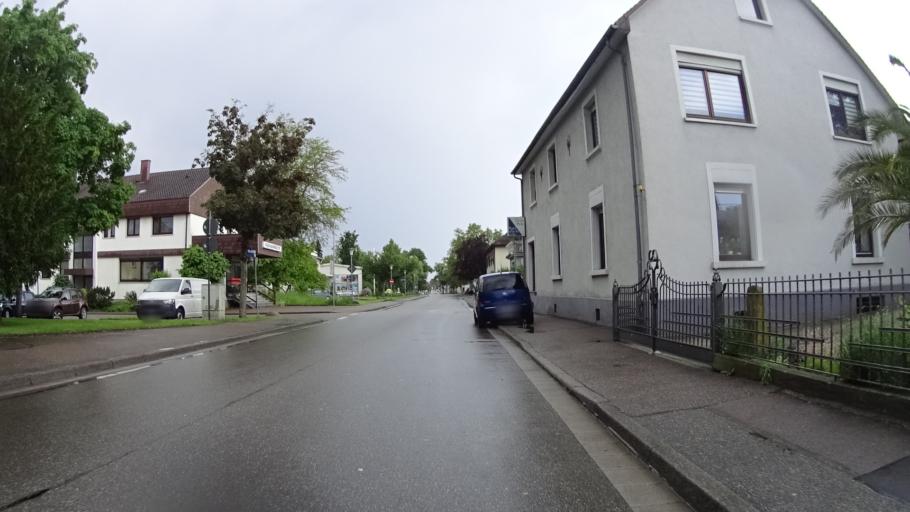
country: DE
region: Baden-Wuerttemberg
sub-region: Karlsruhe Region
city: Durmersheim
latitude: 48.9333
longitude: 8.2719
